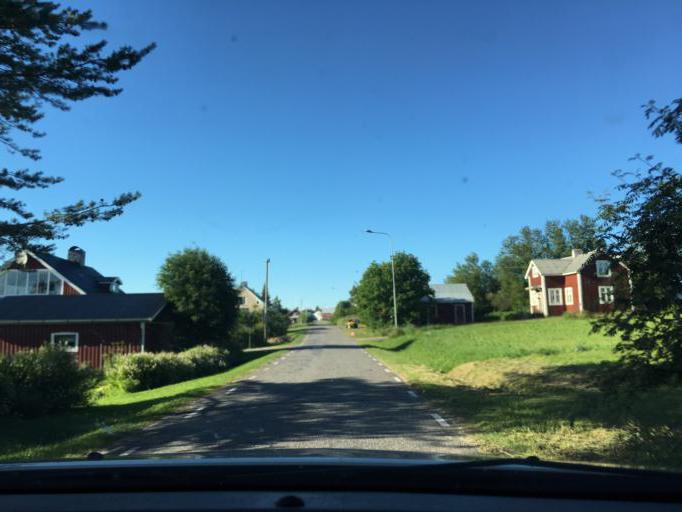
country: SE
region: Norrbotten
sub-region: Kalix Kommun
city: Toere
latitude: 66.1034
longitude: 22.7811
